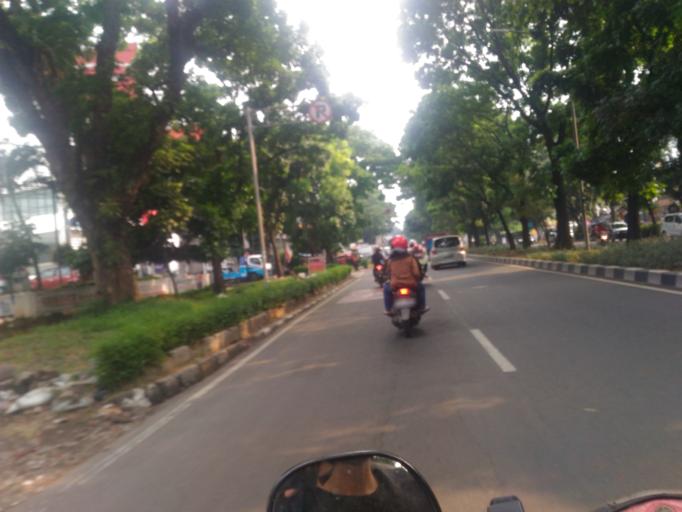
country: ID
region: West Java
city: Bogor
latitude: -6.5769
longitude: 106.8076
